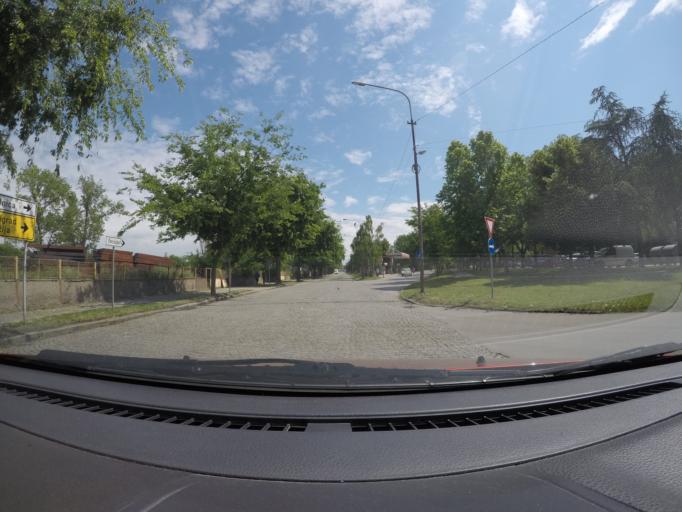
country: RS
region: Autonomna Pokrajina Vojvodina
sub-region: Srednjebanatski Okrug
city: Zrenjanin
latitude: 45.3813
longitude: 20.3762
